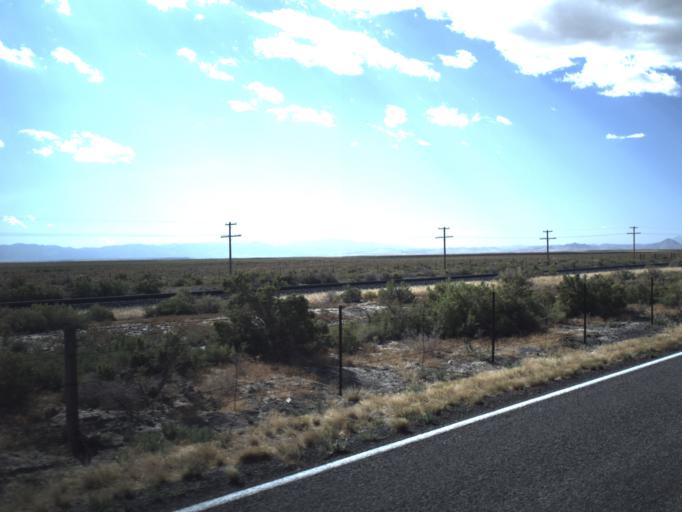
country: US
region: Utah
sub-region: Millard County
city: Delta
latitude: 39.0470
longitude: -112.7688
